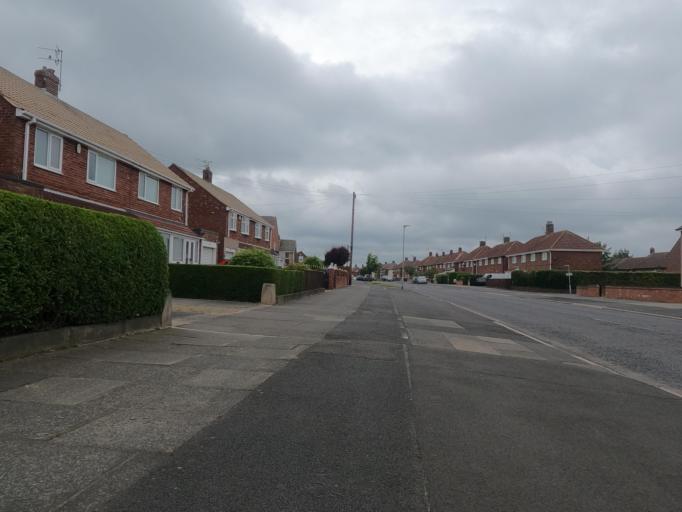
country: GB
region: England
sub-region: Northumberland
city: Blyth
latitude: 55.1242
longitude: -1.5404
